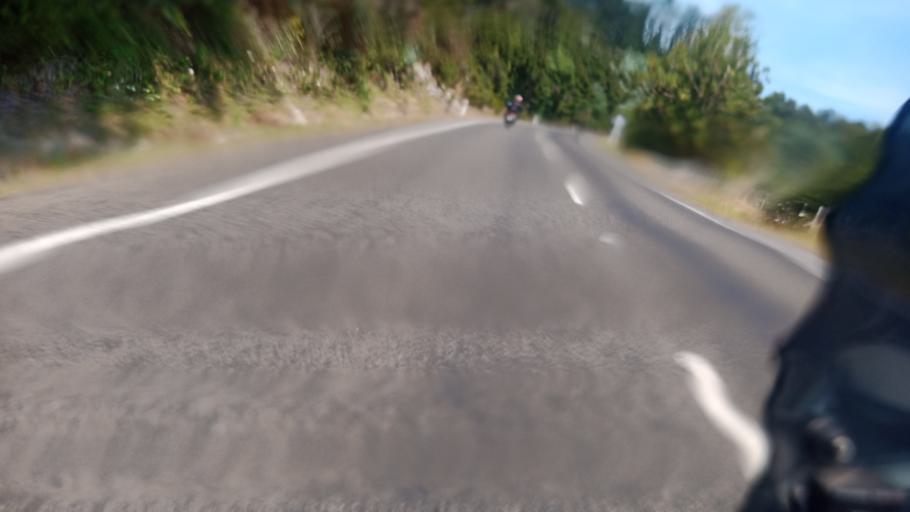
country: NZ
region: Bay of Plenty
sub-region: Opotiki District
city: Opotiki
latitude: -37.5916
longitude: 178.2406
